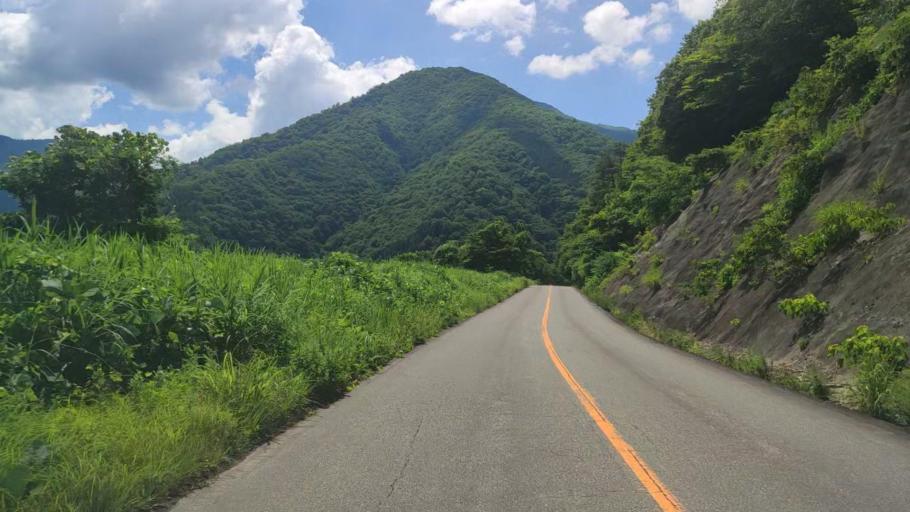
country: JP
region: Fukui
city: Ono
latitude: 35.9060
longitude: 136.5321
